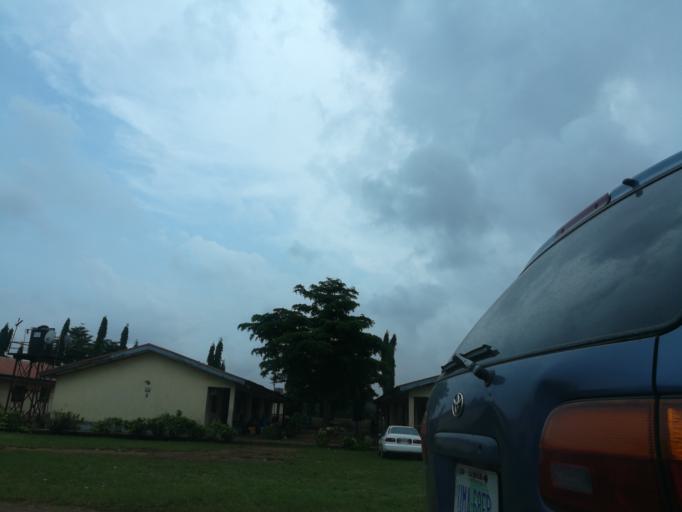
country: NG
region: Lagos
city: Oshodi
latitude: 6.5649
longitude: 3.3515
